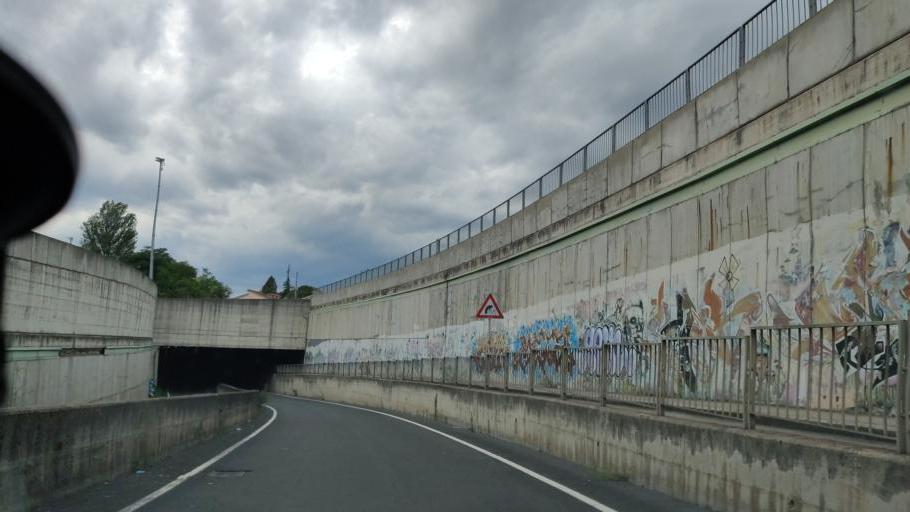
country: IT
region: Umbria
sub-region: Provincia di Terni
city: Terni
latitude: 42.5701
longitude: 12.6444
